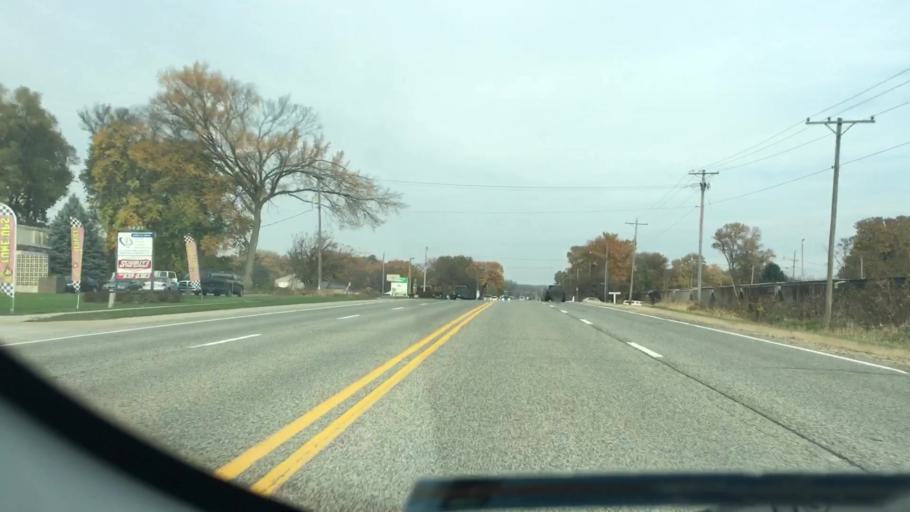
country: US
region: Illinois
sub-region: Peoria County
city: Peoria Heights
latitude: 40.7526
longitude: -89.5612
